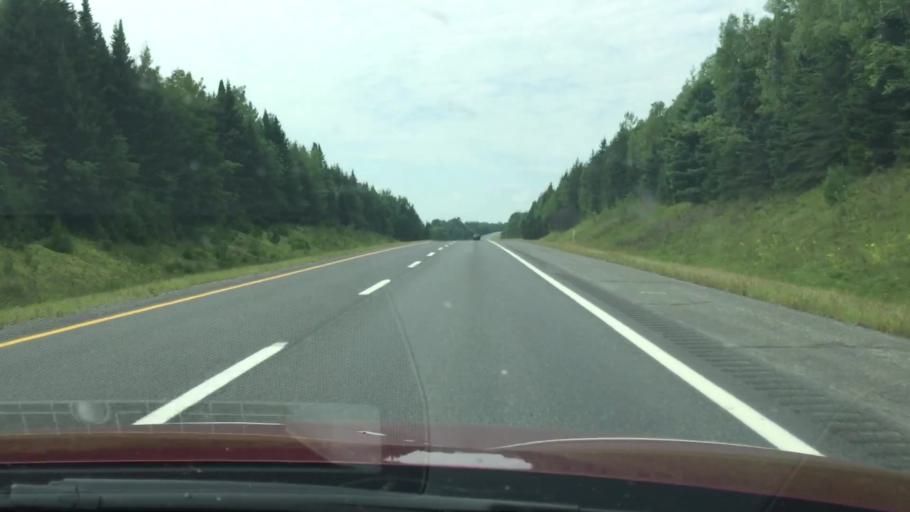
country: US
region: Maine
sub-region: Aroostook County
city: Hodgdon
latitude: 46.1407
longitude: -68.0036
